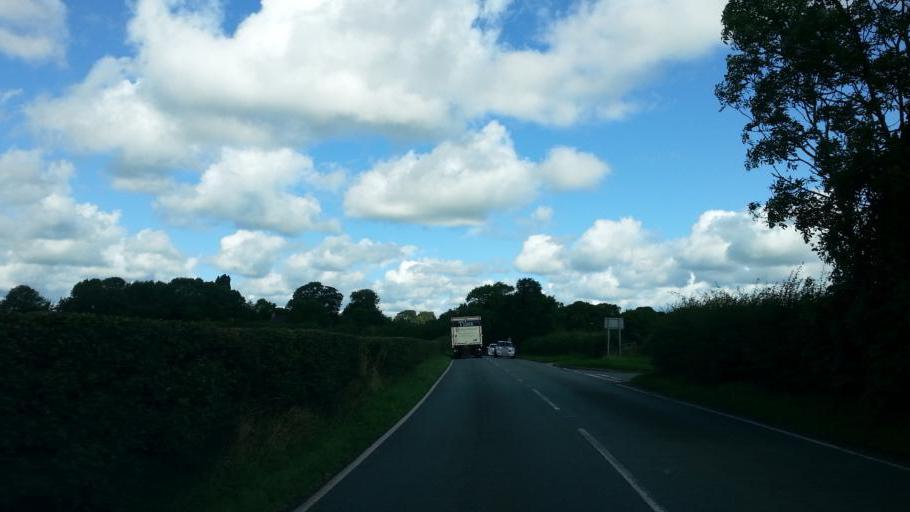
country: GB
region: England
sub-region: Staffordshire
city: Uttoxeter
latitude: 52.8842
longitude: -1.8815
